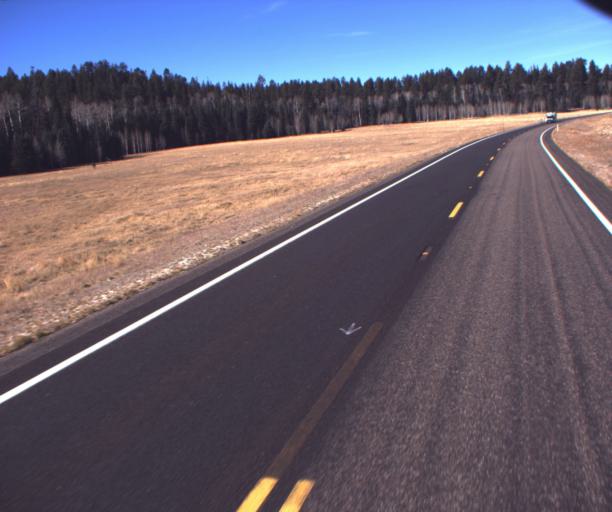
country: US
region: Arizona
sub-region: Coconino County
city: Grand Canyon
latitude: 36.5276
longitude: -112.1490
